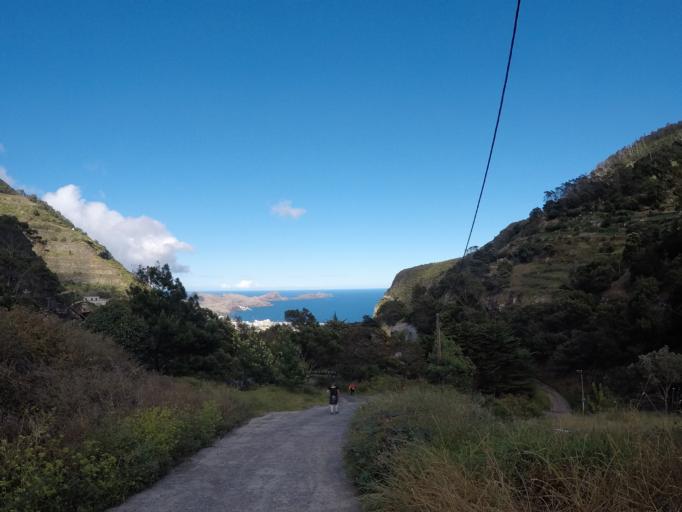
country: PT
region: Madeira
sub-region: Machico
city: Canical
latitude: 32.7373
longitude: -16.7582
